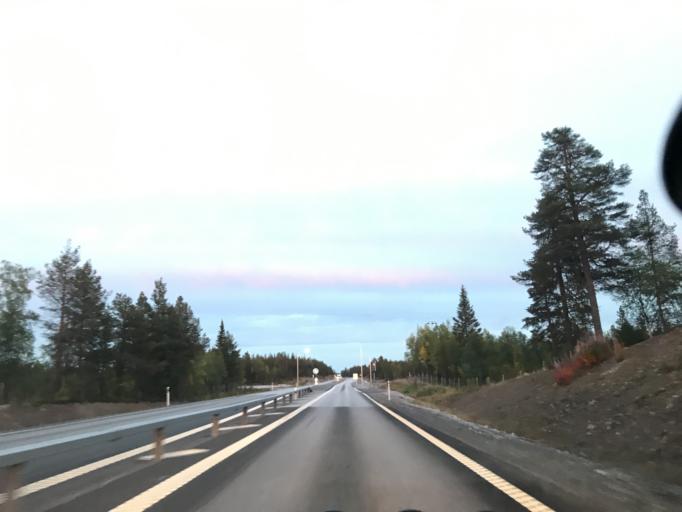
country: SE
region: Norrbotten
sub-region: Gallivare Kommun
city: Malmberget
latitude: 67.6704
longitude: 20.9499
